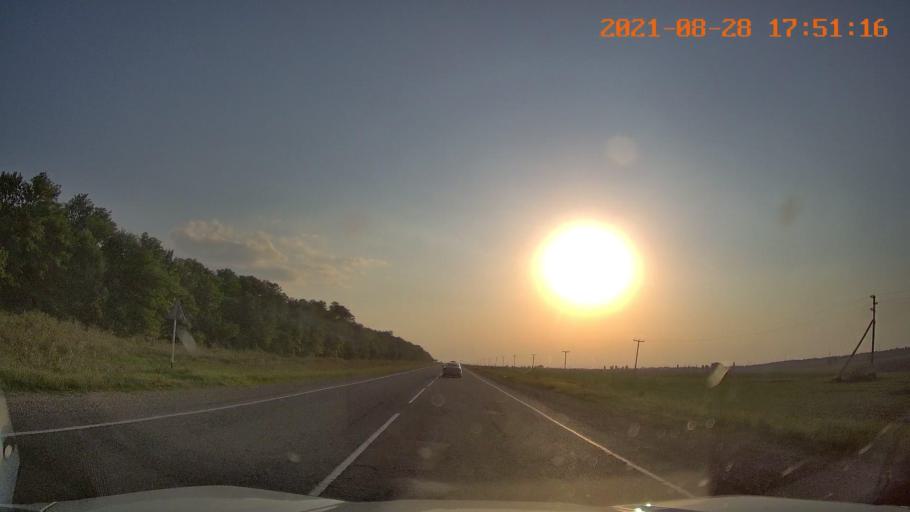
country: RU
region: Krasnodarskiy
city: Konstantinovskaya
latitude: 44.9446
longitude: 40.7984
